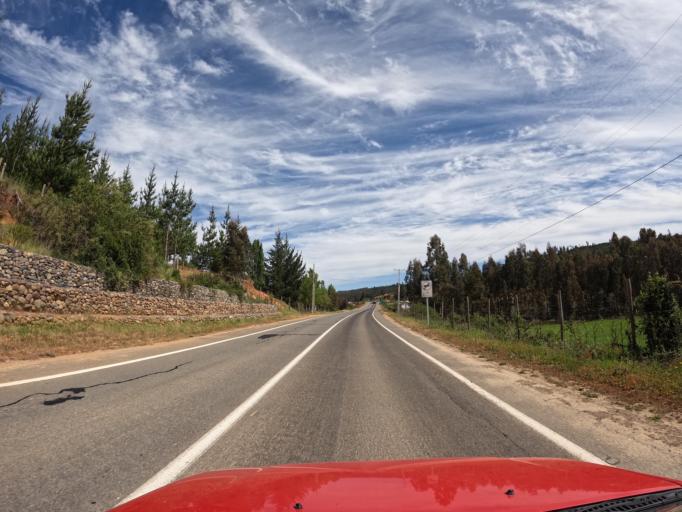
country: CL
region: Maule
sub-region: Provincia de Talca
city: Talca
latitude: -35.1415
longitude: -71.9637
